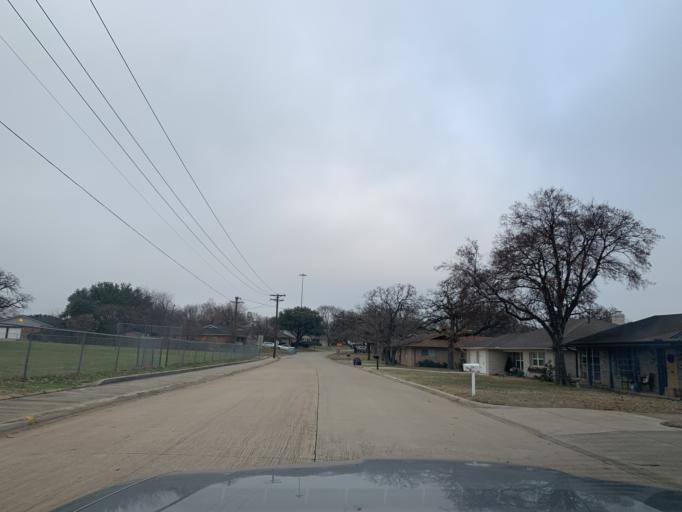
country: US
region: Texas
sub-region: Tarrant County
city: Bedford
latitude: 32.8373
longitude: -97.1572
